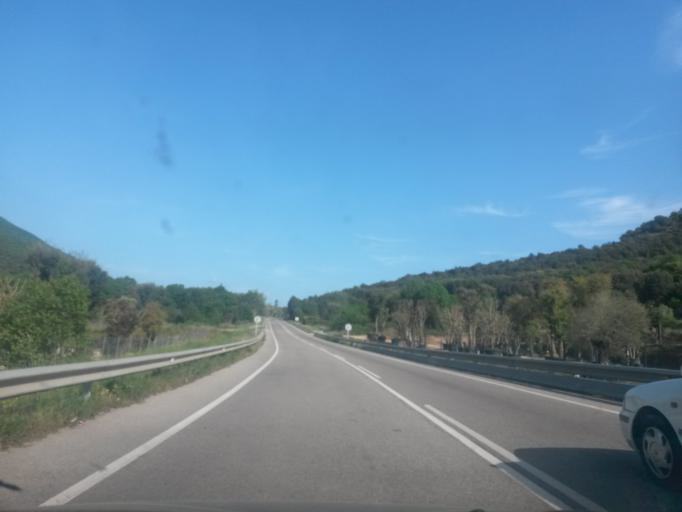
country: ES
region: Catalonia
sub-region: Provincia de Girona
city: les Planes d'Hostoles
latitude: 42.0659
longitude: 2.5298
